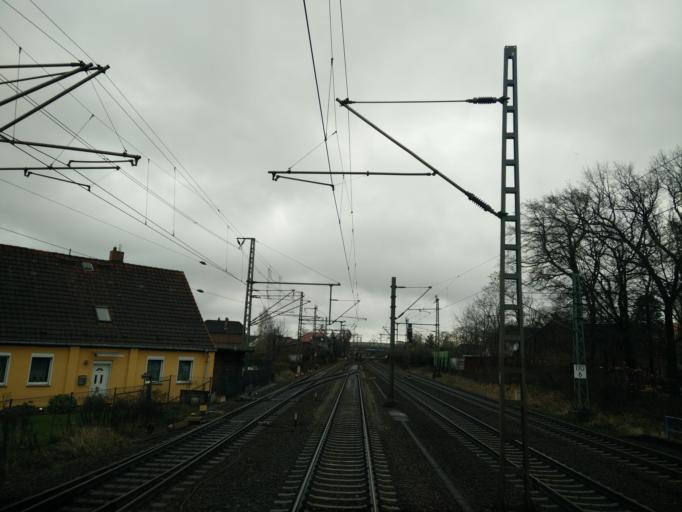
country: DE
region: Mecklenburg-Vorpommern
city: Ludwigslust
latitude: 53.3340
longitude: 11.4961
